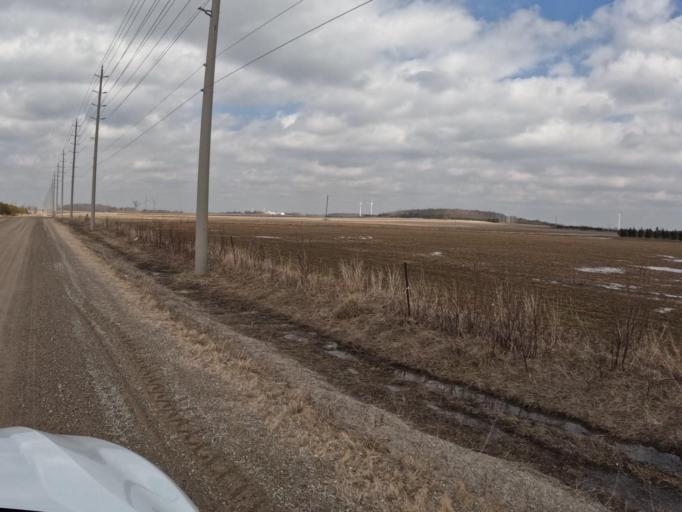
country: CA
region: Ontario
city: Shelburne
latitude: 44.0440
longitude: -80.3184
